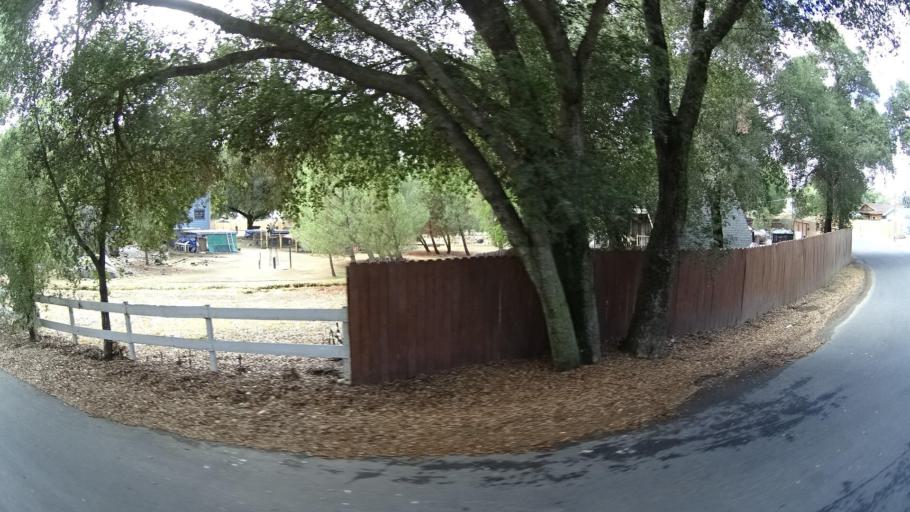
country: US
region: California
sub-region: San Diego County
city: Campo
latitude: 32.6826
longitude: -116.5127
